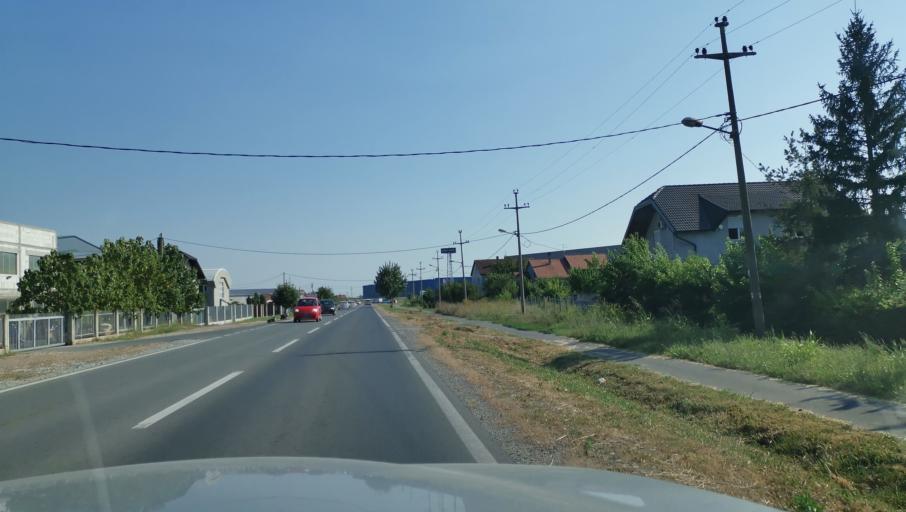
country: RS
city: Ugrinovci
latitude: 44.8570
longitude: 20.2052
